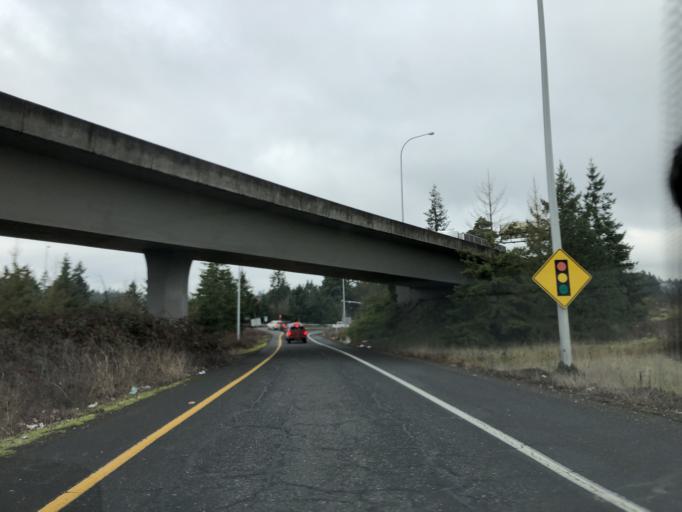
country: US
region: Washington
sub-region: Clark County
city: Vancouver
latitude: 45.6485
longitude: -122.6609
